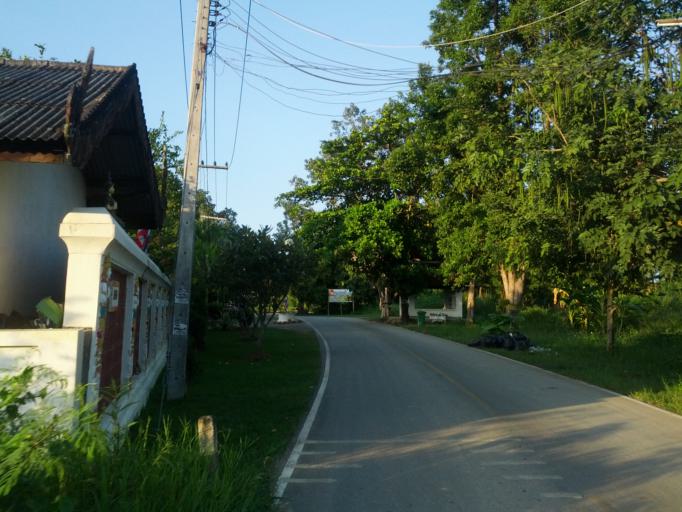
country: TH
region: Chiang Mai
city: San Kamphaeng
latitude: 18.7657
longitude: 99.0989
